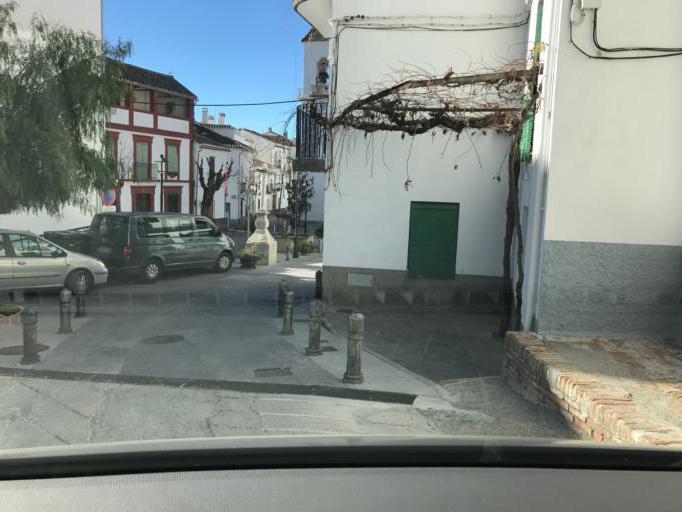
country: ES
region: Andalusia
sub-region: Provincia de Granada
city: Viznar
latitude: 37.2315
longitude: -3.5538
